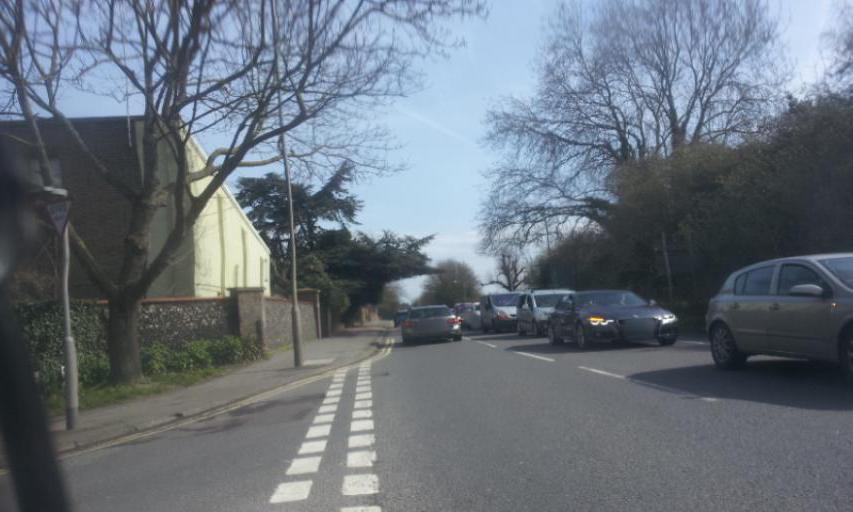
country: GB
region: England
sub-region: Kent
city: Faversham
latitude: 51.3089
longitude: 0.8876
